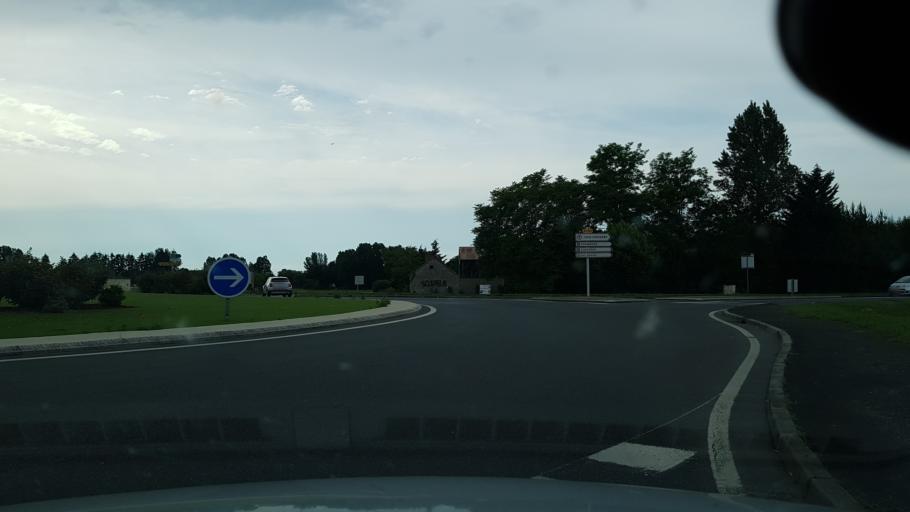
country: FR
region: Centre
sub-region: Departement du Loir-et-Cher
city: Contres
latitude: 47.4311
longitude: 1.4356
